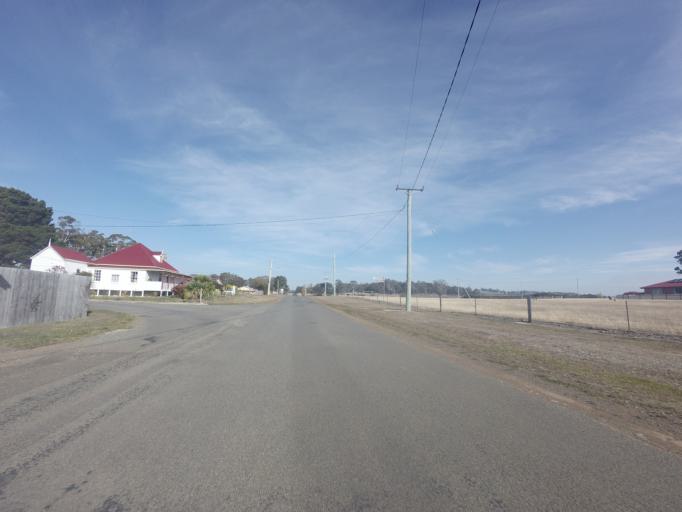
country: AU
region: Tasmania
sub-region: Sorell
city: Sorell
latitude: -42.4567
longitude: 147.4615
